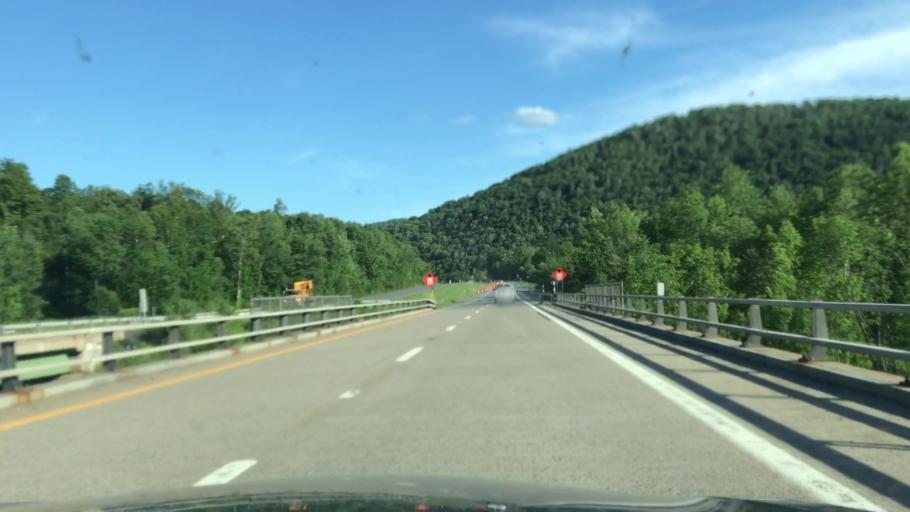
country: US
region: New York
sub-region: Delaware County
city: Walton
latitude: 41.9771
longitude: -75.0537
